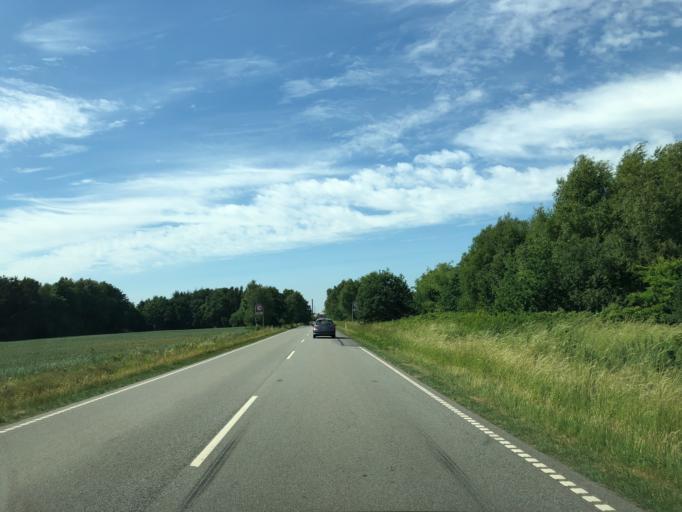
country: DK
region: Central Jutland
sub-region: Ikast-Brande Kommune
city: Brande
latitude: 55.9231
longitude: 9.1622
